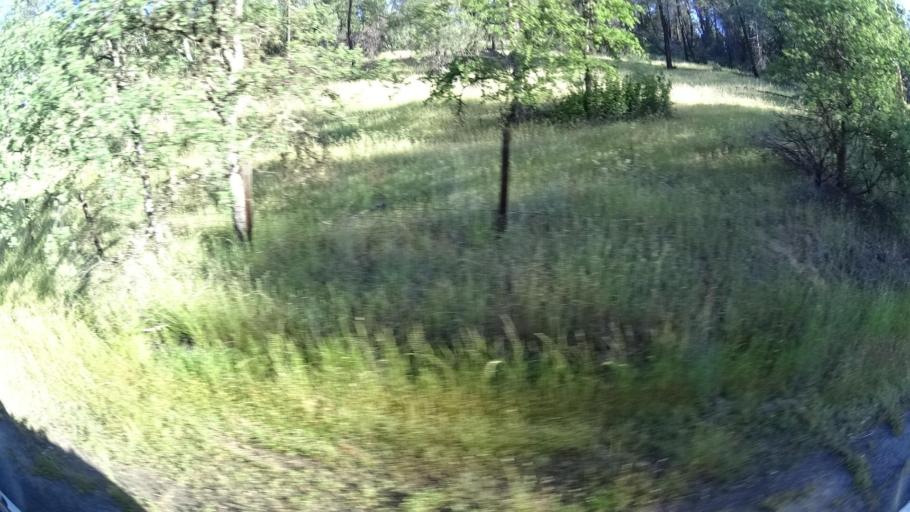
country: US
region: California
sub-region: Lake County
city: Upper Lake
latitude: 39.2080
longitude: -122.9224
